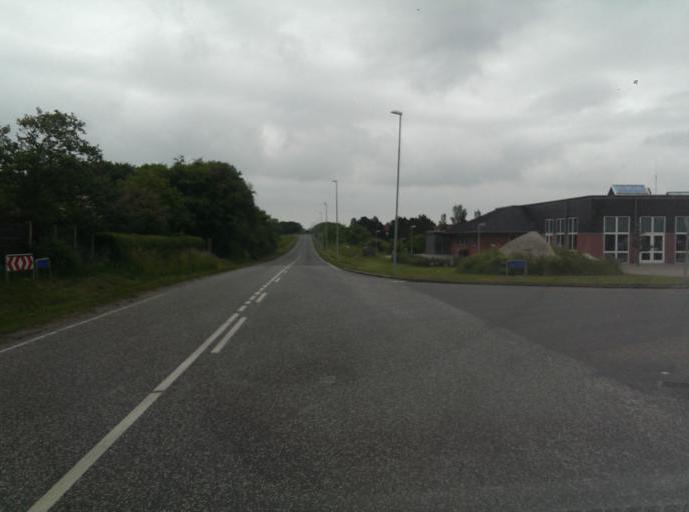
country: DK
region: South Denmark
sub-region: Fano Kommune
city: Nordby
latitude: 55.5269
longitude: 8.3570
